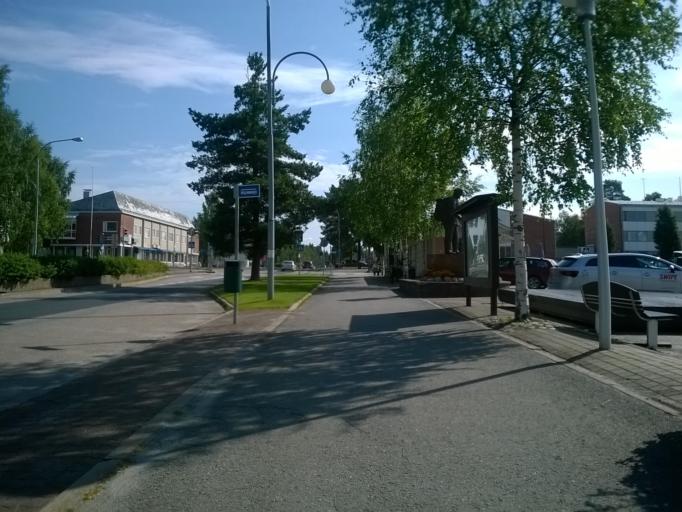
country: FI
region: Kainuu
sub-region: Kehys-Kainuu
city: Kuhmo
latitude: 64.1284
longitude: 29.5206
